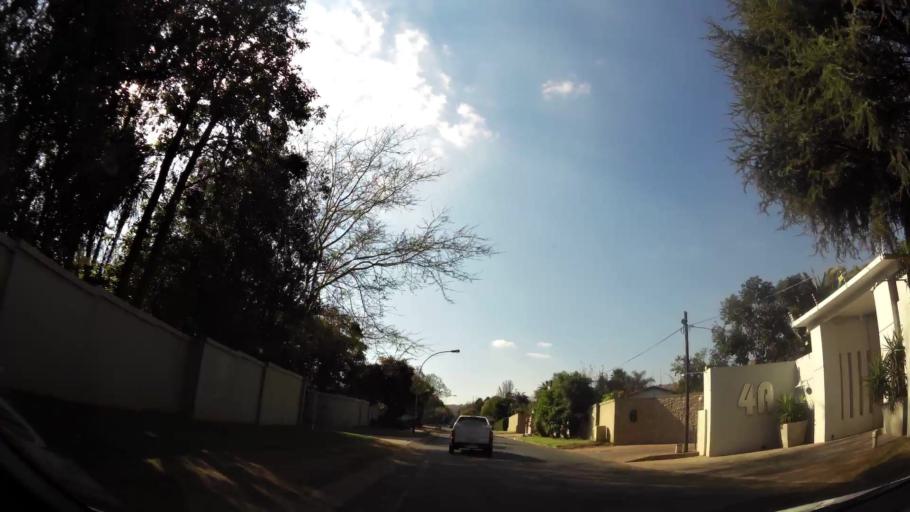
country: ZA
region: Gauteng
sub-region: Ekurhuleni Metropolitan Municipality
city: Germiston
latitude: -26.1808
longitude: 28.1380
